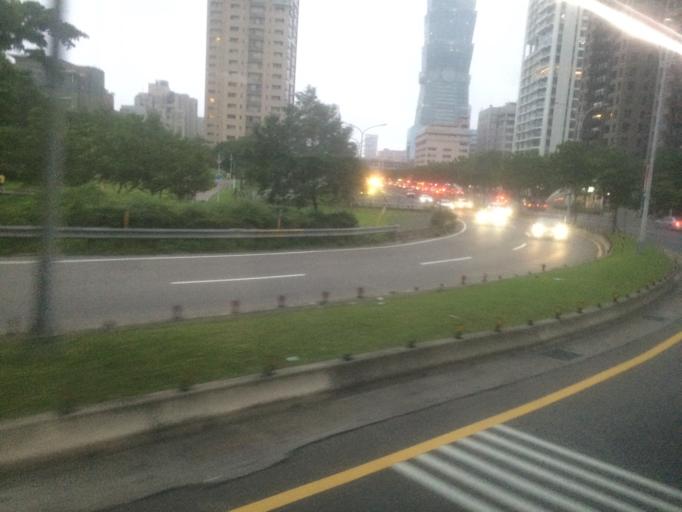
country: TW
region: Taipei
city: Taipei
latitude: 25.0324
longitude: 121.5717
